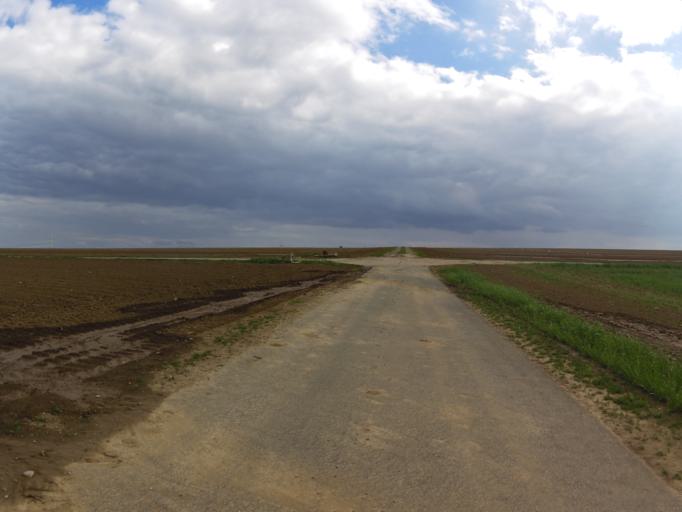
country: DE
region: Bavaria
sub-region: Regierungsbezirk Unterfranken
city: Oberpleichfeld
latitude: 49.8576
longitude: 10.0830
